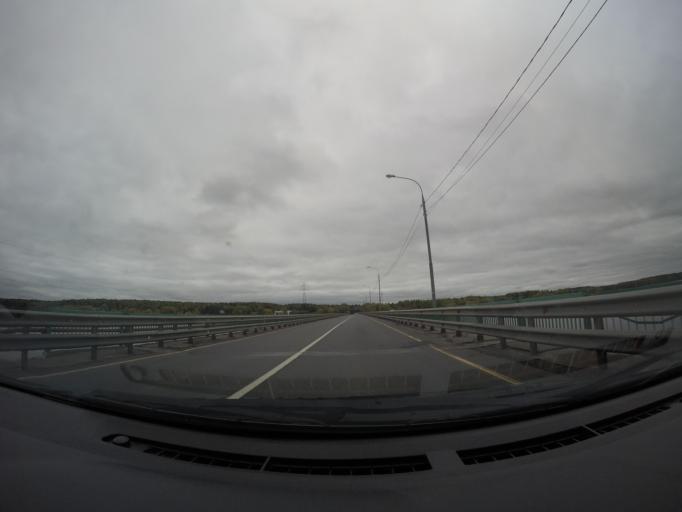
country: RU
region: Moskovskaya
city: Ruza
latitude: 55.7622
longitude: 36.2613
